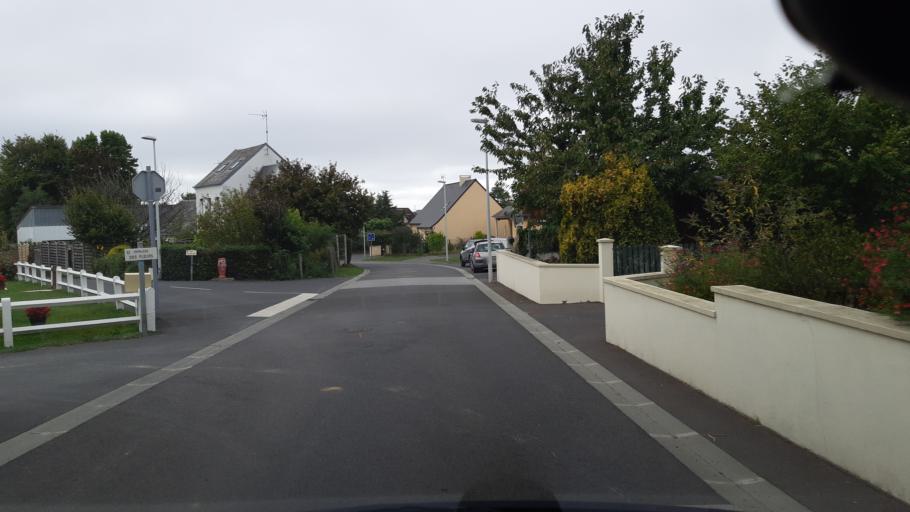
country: FR
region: Lower Normandy
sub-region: Departement de la Manche
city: Saint-Planchers
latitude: 48.8429
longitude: -1.5460
